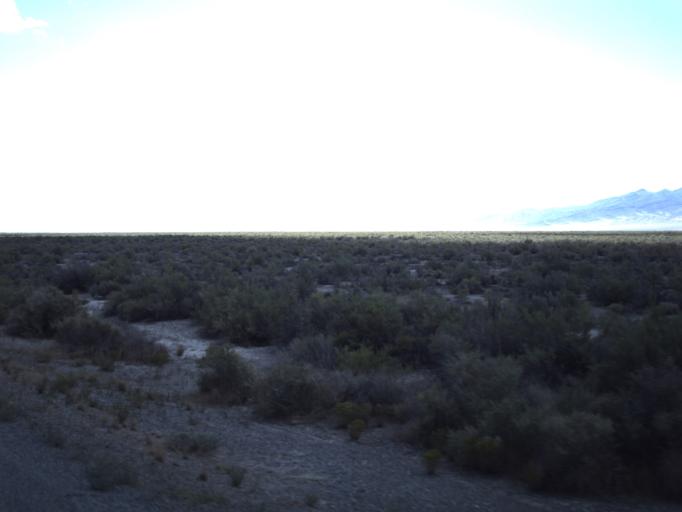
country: US
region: Nevada
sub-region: White Pine County
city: McGill
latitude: 39.0520
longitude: -113.9824
